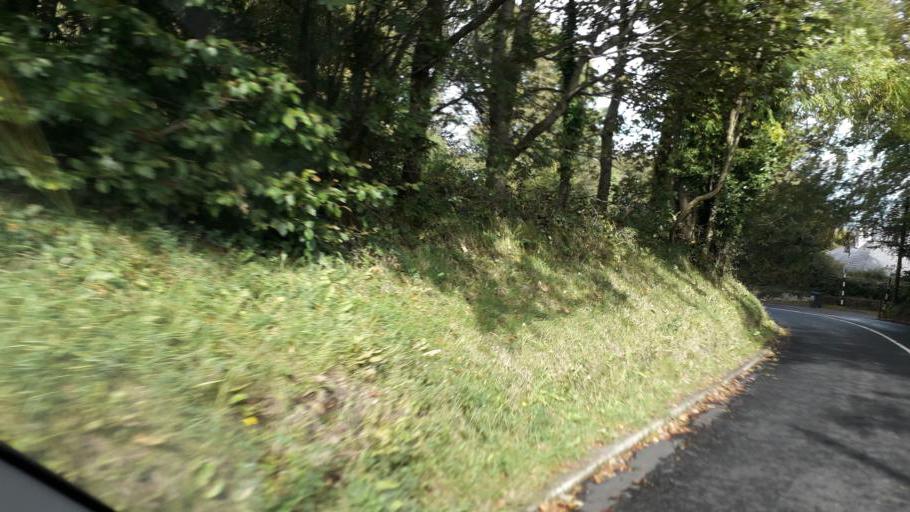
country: IE
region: Leinster
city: Sandyford
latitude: 53.2336
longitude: -6.2215
